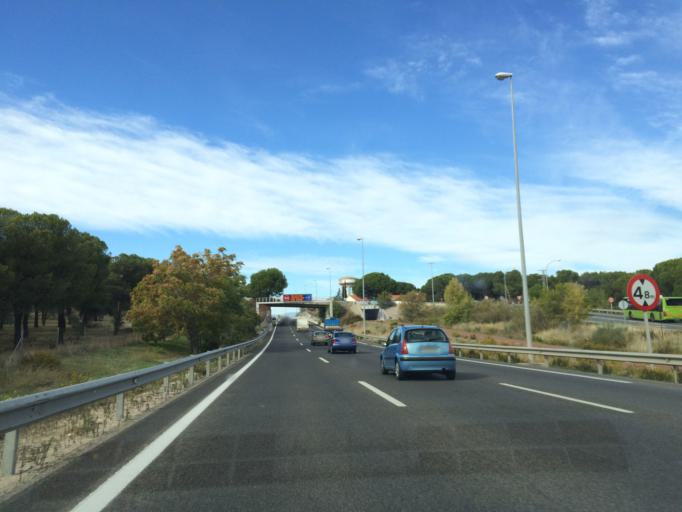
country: ES
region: Madrid
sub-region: Provincia de Madrid
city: Las Tablas
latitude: 40.5355
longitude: -3.6939
